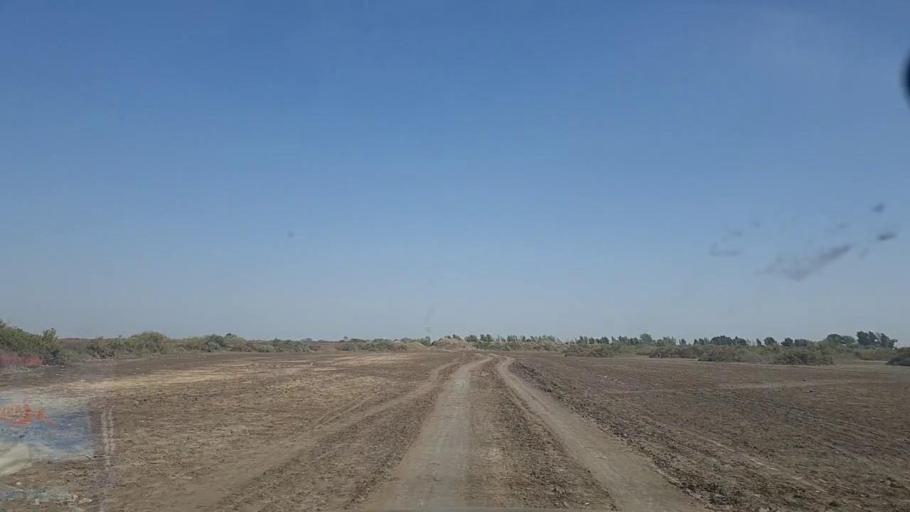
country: PK
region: Sindh
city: Chuhar Jamali
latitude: 24.2721
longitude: 67.7504
